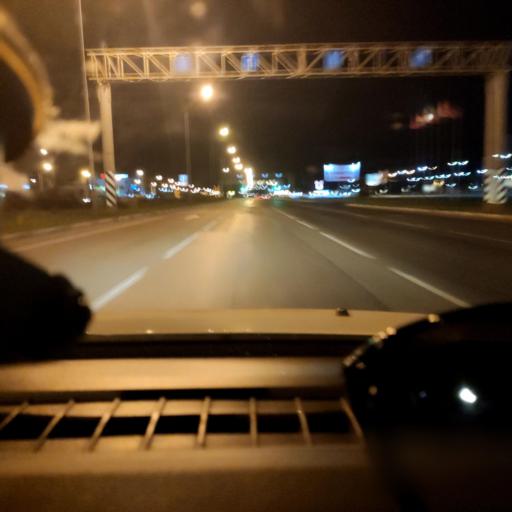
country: RU
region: Samara
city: Samara
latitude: 53.1400
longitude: 50.1777
